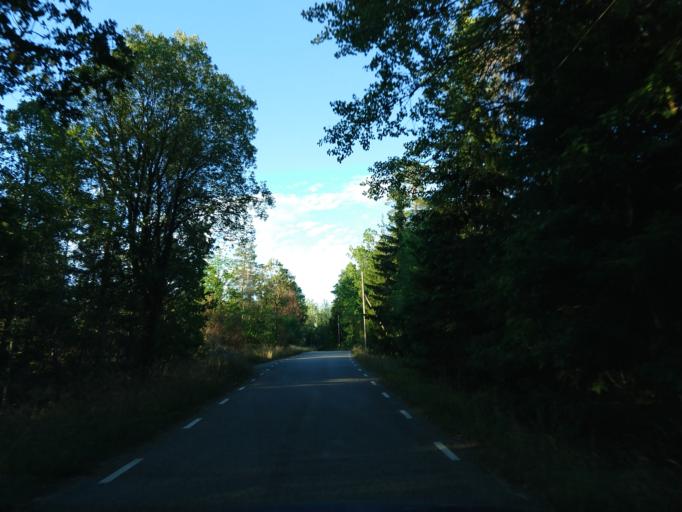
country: SE
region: Blekinge
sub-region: Ronneby Kommun
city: Brakne-Hoby
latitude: 56.2755
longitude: 15.1626
